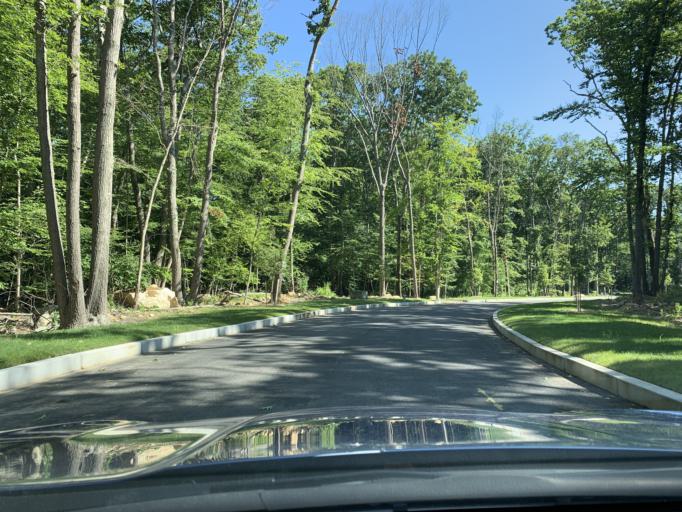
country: US
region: Rhode Island
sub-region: Washington County
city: Exeter
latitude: 41.6211
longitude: -71.5196
